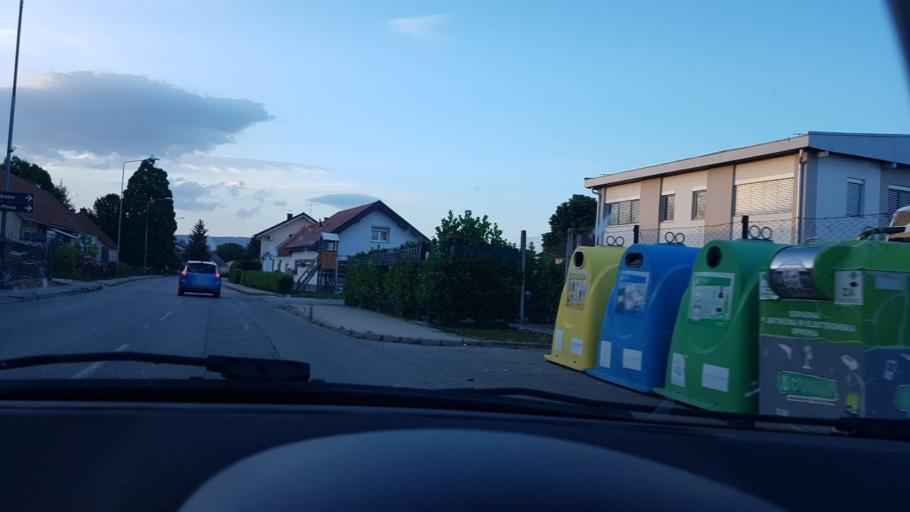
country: SI
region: Brezice
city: Brezice
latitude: 45.9131
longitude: 15.5906
